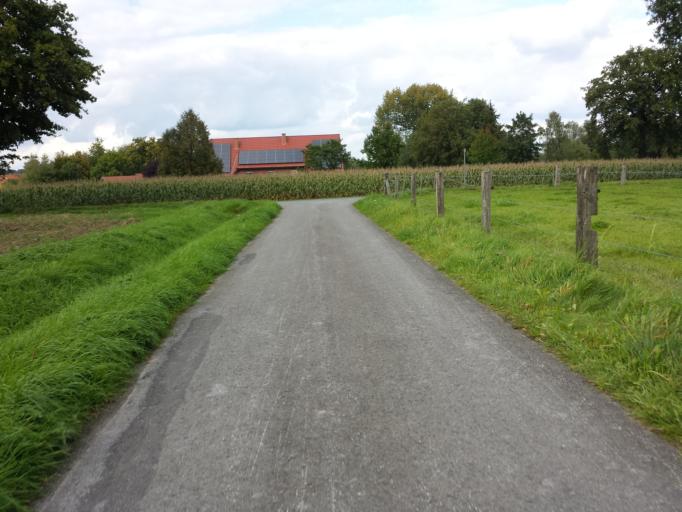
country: DE
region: North Rhine-Westphalia
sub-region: Regierungsbezirk Detmold
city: Langenberg
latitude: 51.7856
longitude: 8.3062
